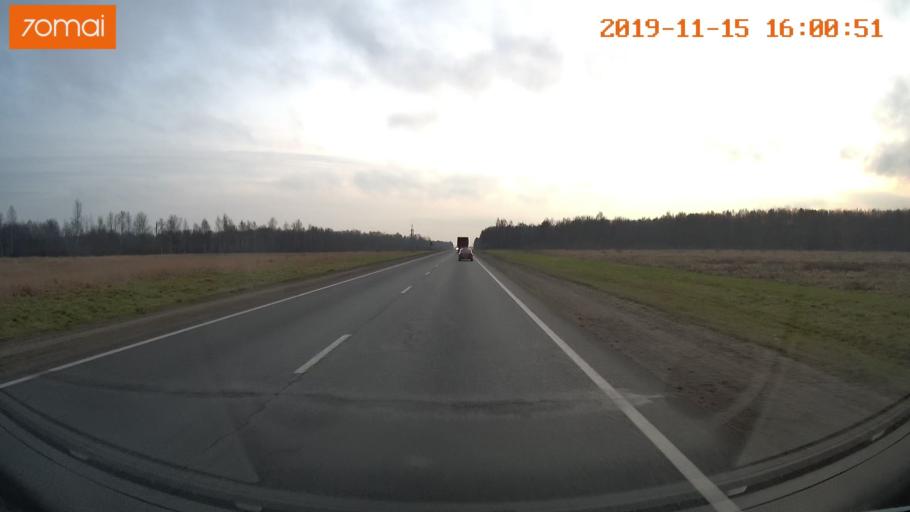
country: RU
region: Jaroslavl
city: Yaroslavl
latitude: 57.7909
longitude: 39.9360
